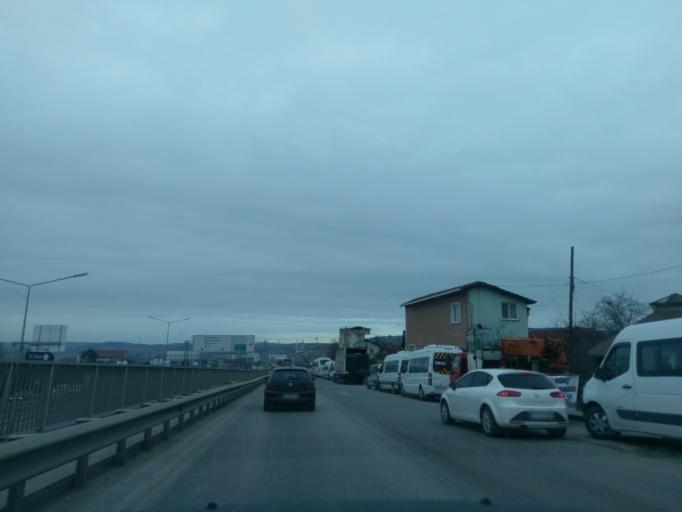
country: TR
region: Istanbul
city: Umraniye
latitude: 41.0963
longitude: 29.0971
